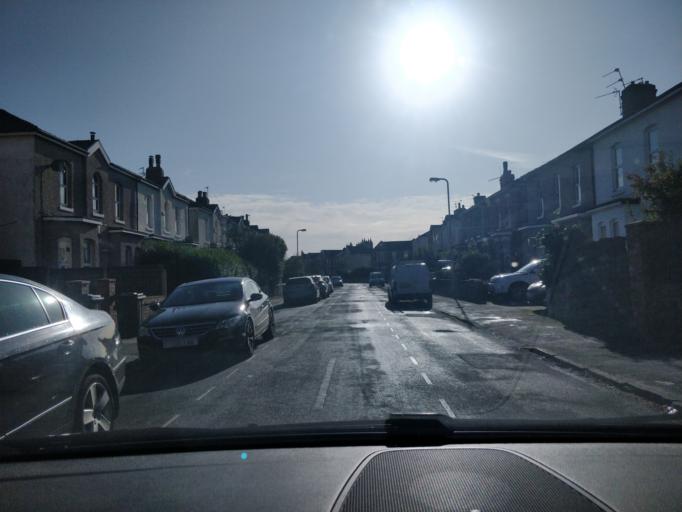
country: GB
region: England
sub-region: Sefton
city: Southport
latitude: 53.6429
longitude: -2.9986
